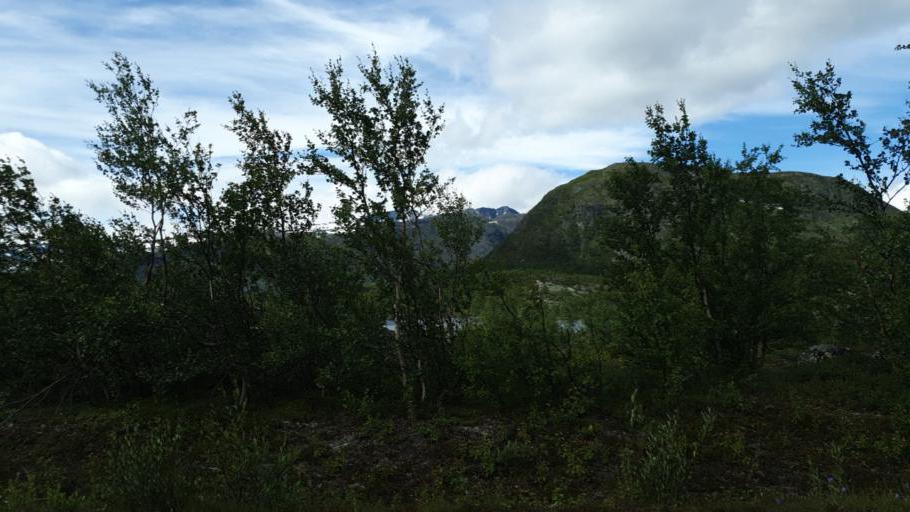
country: NO
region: Oppland
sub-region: Oystre Slidre
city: Heggenes
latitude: 61.4868
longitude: 8.8303
